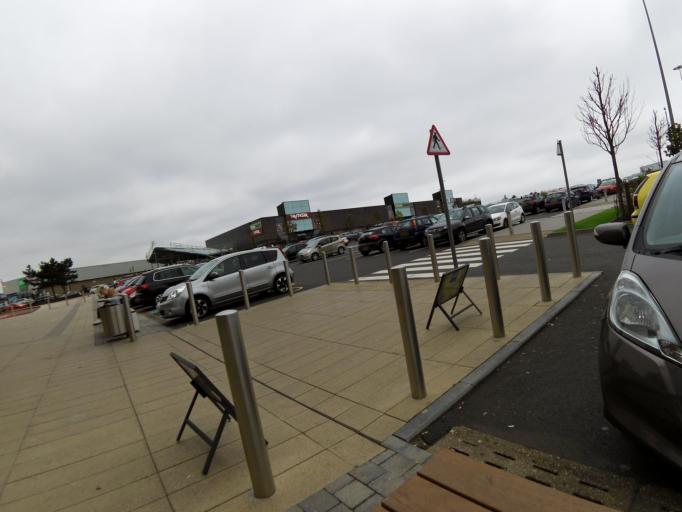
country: GB
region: Scotland
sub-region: East Lothian
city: Musselburgh
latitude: 55.9348
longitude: -3.1011
